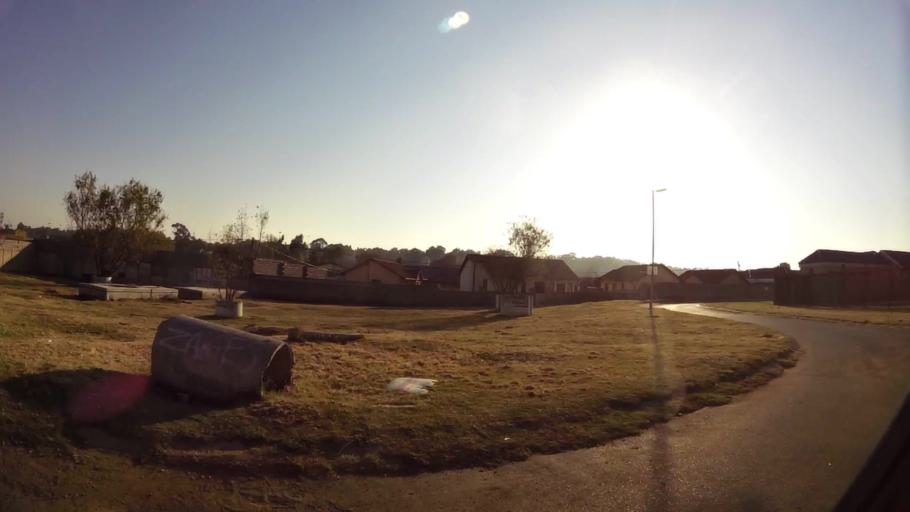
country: ZA
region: Gauteng
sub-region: City of Johannesburg Metropolitan Municipality
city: Soweto
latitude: -26.2776
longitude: 27.9658
